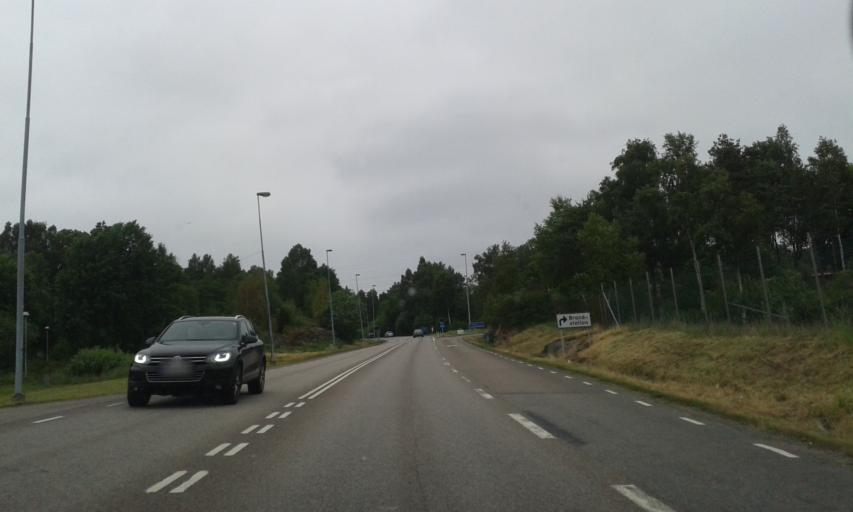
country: SE
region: Vaestra Goetaland
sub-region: Kungalvs Kommun
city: Kungalv
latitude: 57.8789
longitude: 11.9714
